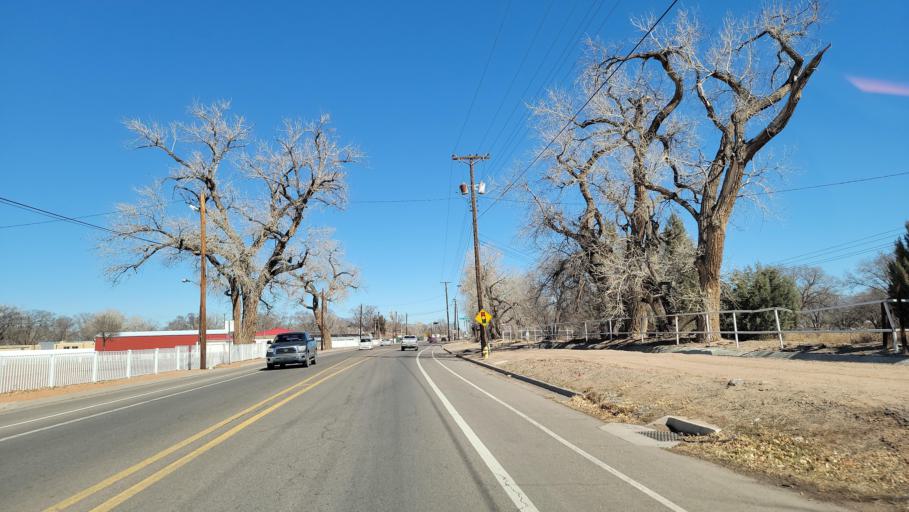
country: US
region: New Mexico
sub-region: Bernalillo County
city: South Valley
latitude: 35.0100
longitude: -106.6878
